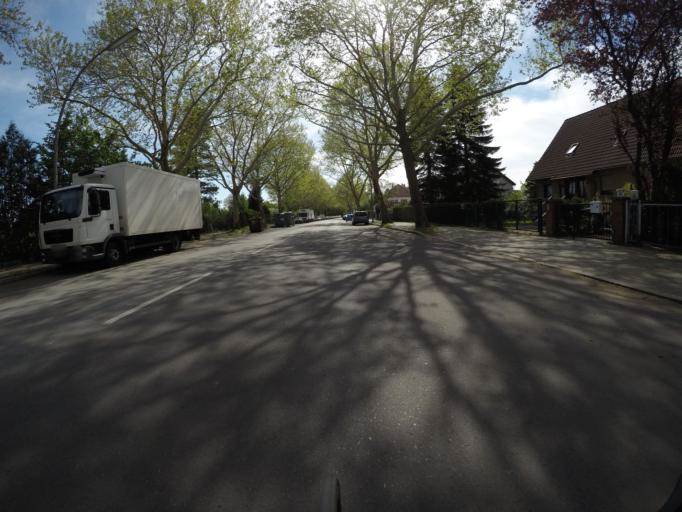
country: DE
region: Berlin
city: Marienfelde
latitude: 52.4168
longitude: 13.3854
